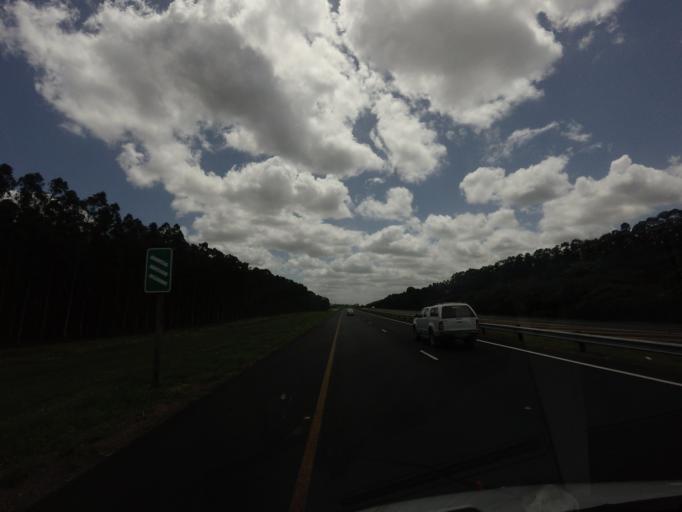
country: ZA
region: KwaZulu-Natal
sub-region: uThungulu District Municipality
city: KwaMbonambi
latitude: -28.5318
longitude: 32.1343
